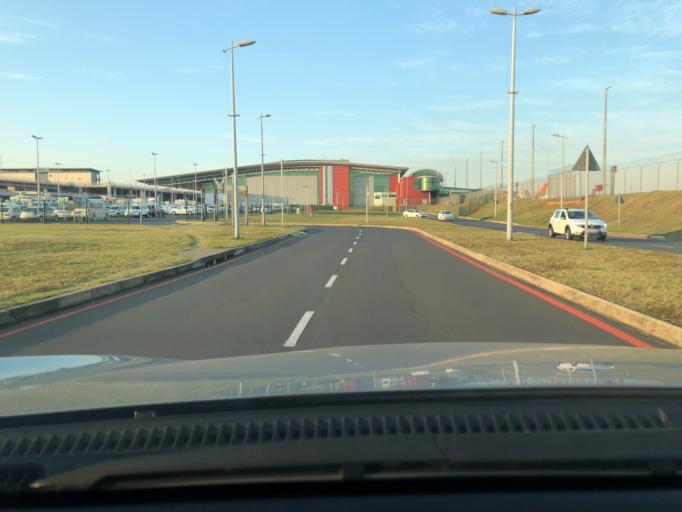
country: ZA
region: KwaZulu-Natal
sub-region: iLembe District Municipality
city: Ballitoville
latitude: -29.6221
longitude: 31.1028
